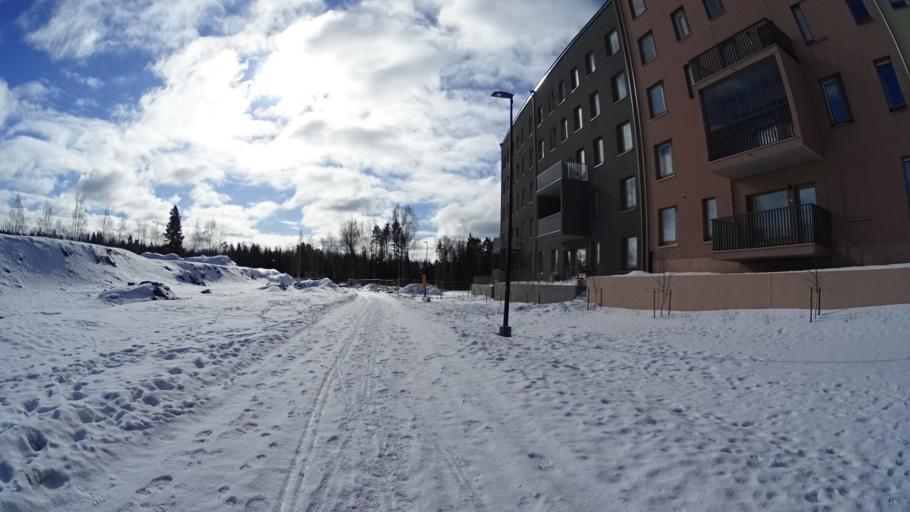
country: FI
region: Uusimaa
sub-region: Helsinki
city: Teekkarikylae
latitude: 60.2614
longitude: 24.8937
